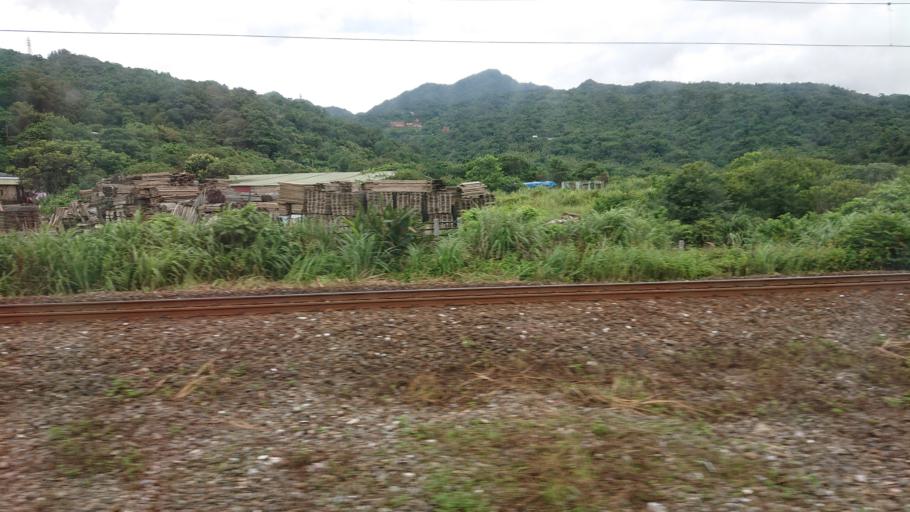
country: TW
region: Taiwan
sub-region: Keelung
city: Keelung
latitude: 25.1057
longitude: 121.8259
